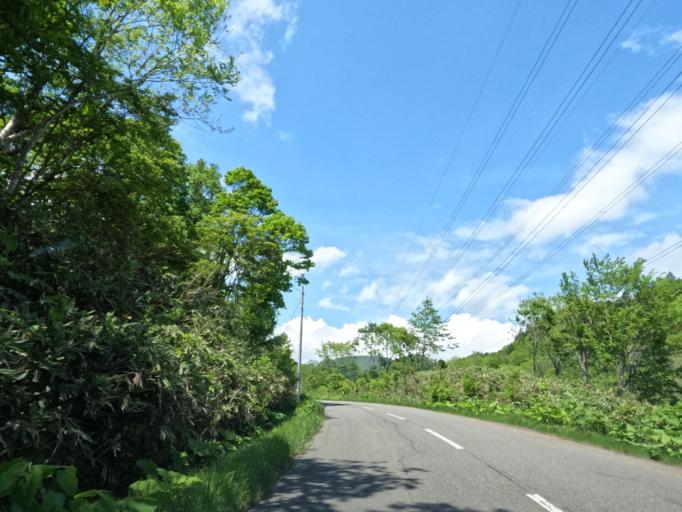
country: JP
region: Hokkaido
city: Takikawa
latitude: 43.5450
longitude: 141.6169
